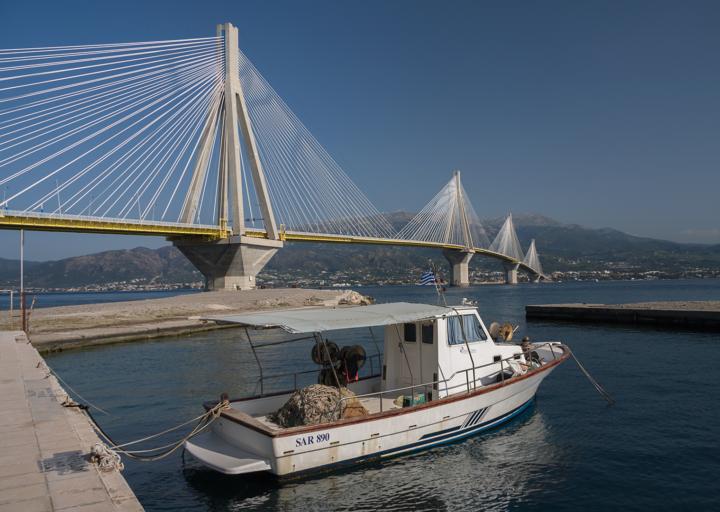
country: GR
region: West Greece
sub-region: Nomos Aitolias kai Akarnanias
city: Antirrio
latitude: 38.3289
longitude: 21.7663
